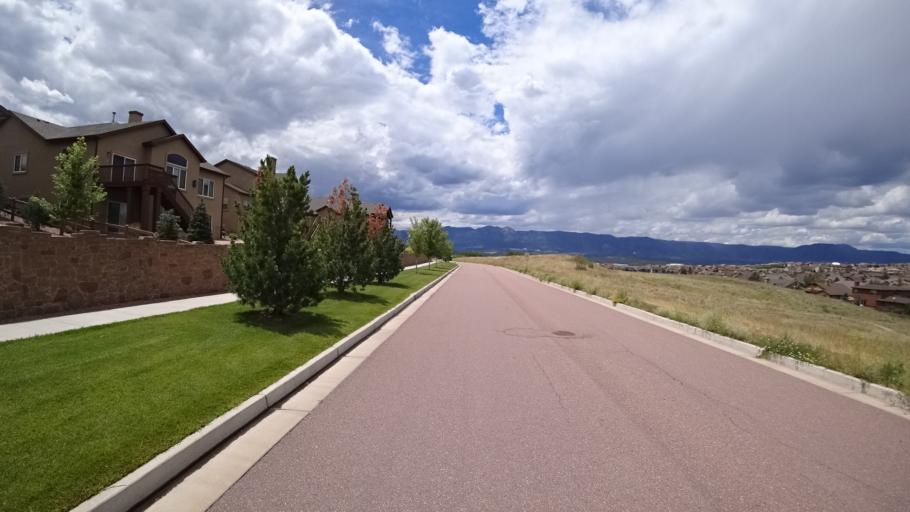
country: US
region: Colorado
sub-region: El Paso County
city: Gleneagle
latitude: 39.0234
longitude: -104.8017
